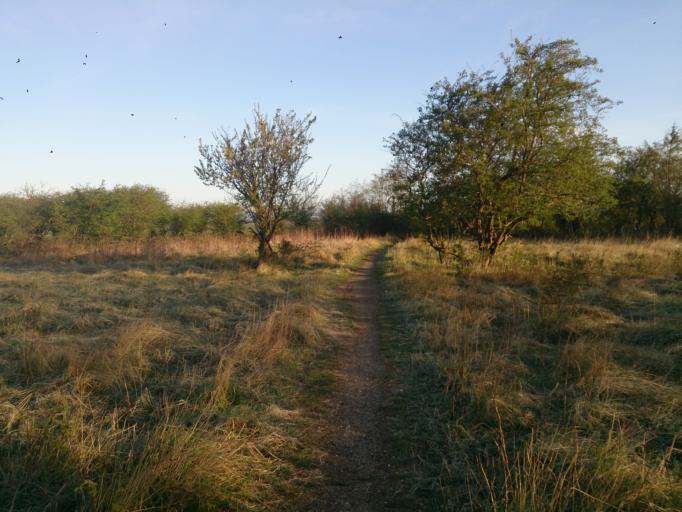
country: DK
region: Capital Region
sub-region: Tarnby Kommune
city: Tarnby
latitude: 55.6024
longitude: 12.5742
